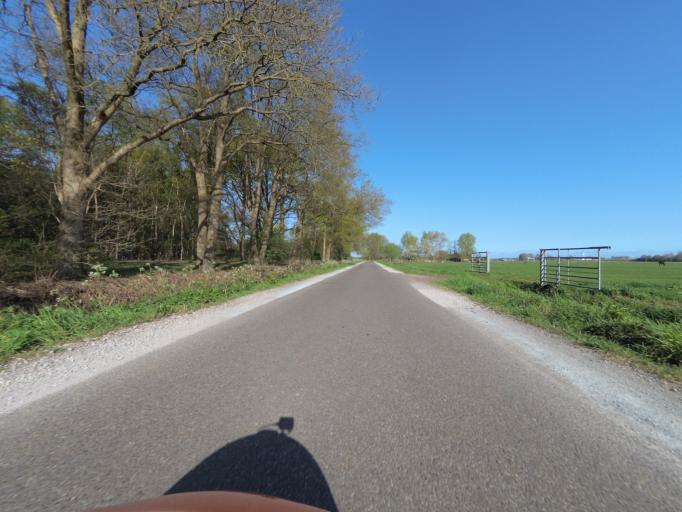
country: NL
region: North Holland
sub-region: Gemeente Naarden
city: Naarden
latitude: 52.2976
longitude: 5.1358
